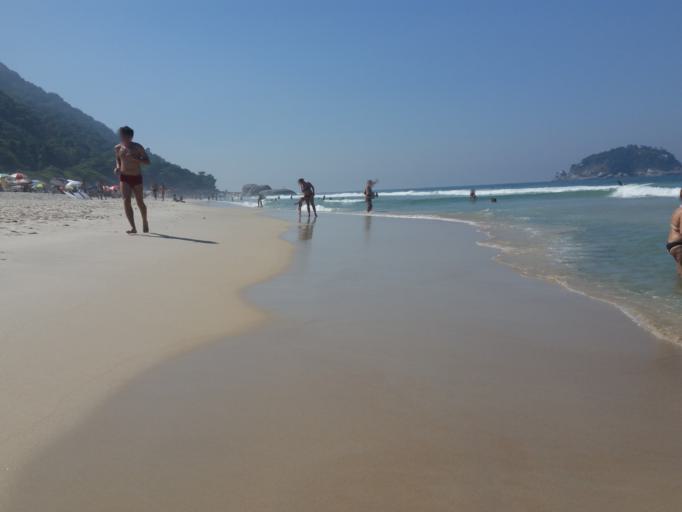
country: BR
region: Rio de Janeiro
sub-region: Nilopolis
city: Nilopolis
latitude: -23.0483
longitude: -43.5193
